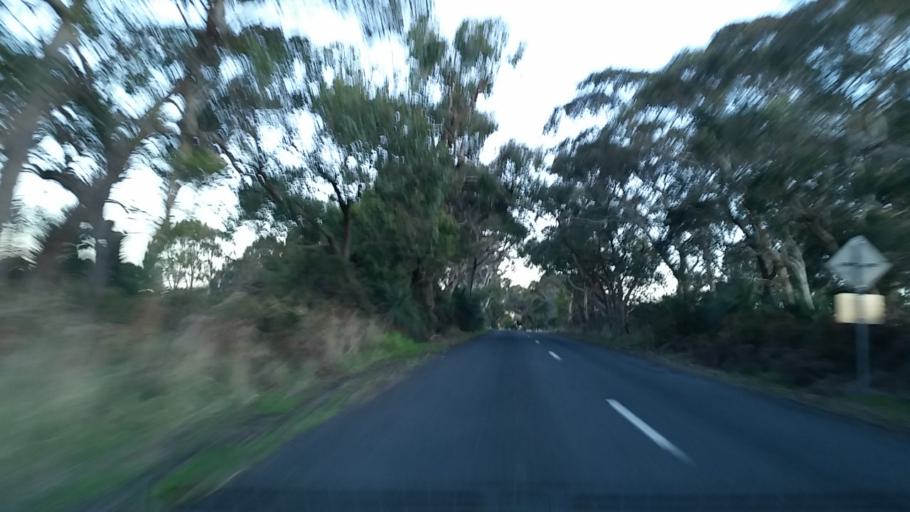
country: AU
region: South Australia
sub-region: Alexandrina
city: Mount Compass
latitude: -35.2907
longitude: 138.6089
